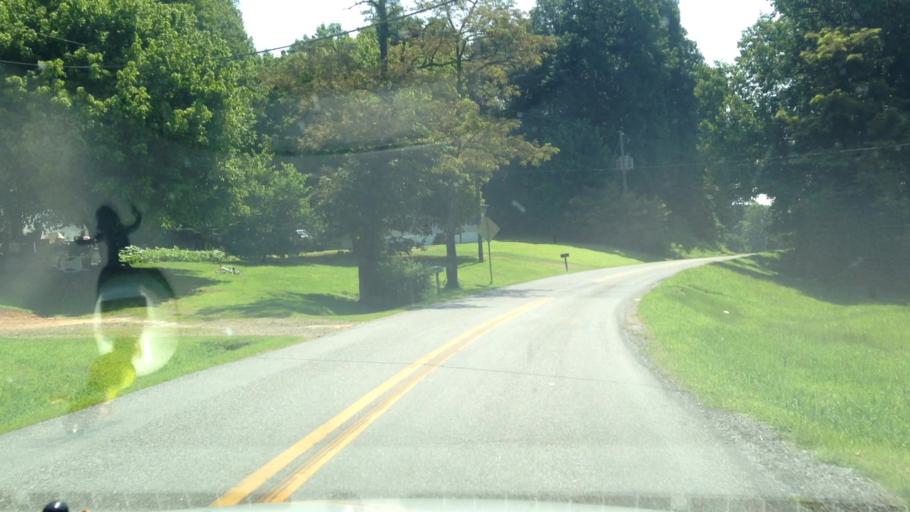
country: US
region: Virginia
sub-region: Patrick County
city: Stuart
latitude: 36.5794
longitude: -80.2668
